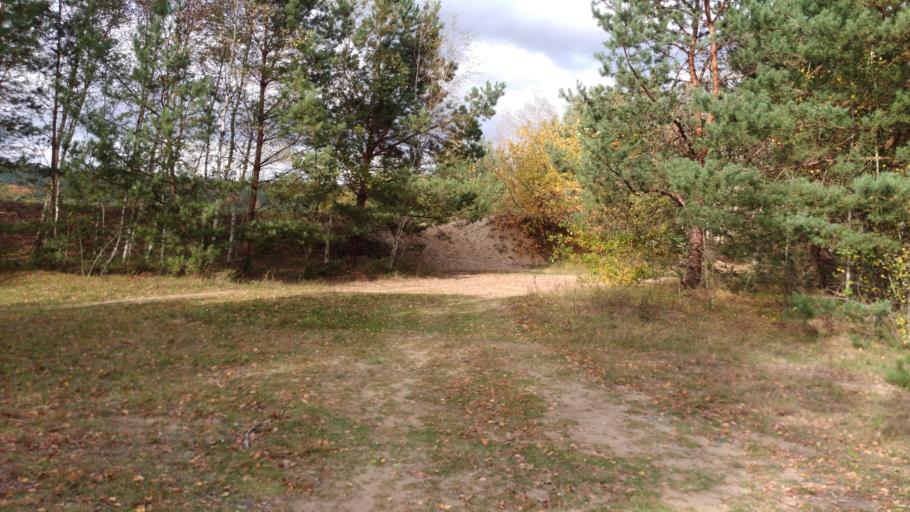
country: DE
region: Saxony
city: Albertstadt
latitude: 51.1014
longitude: 13.7491
